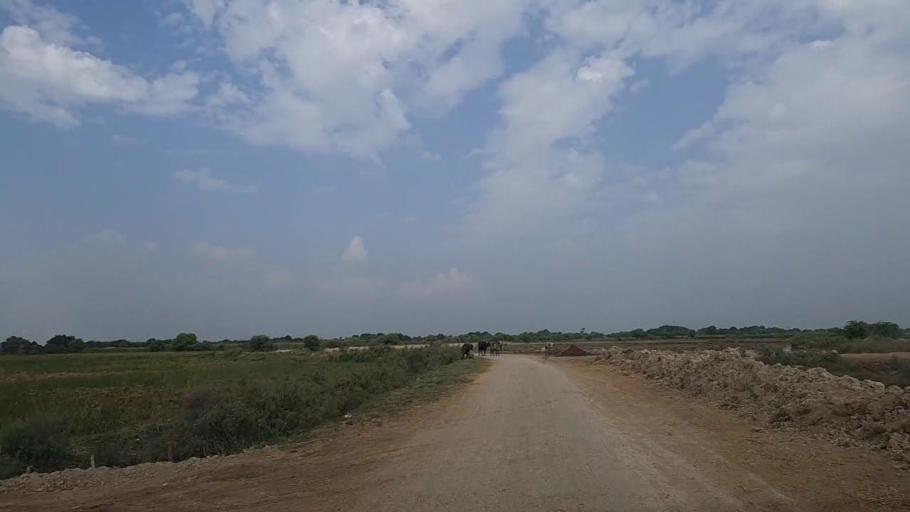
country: PK
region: Sindh
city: Daro Mehar
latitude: 24.7112
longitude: 68.1524
